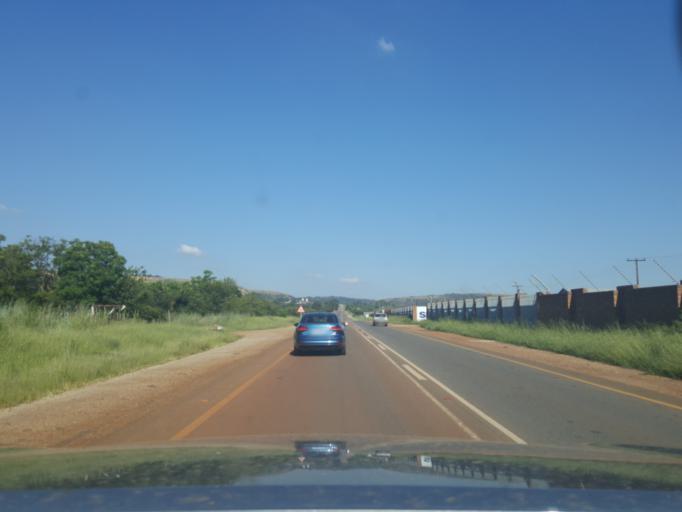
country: ZA
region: Gauteng
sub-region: City of Tshwane Metropolitan Municipality
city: Cullinan
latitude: -25.7667
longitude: 28.4316
